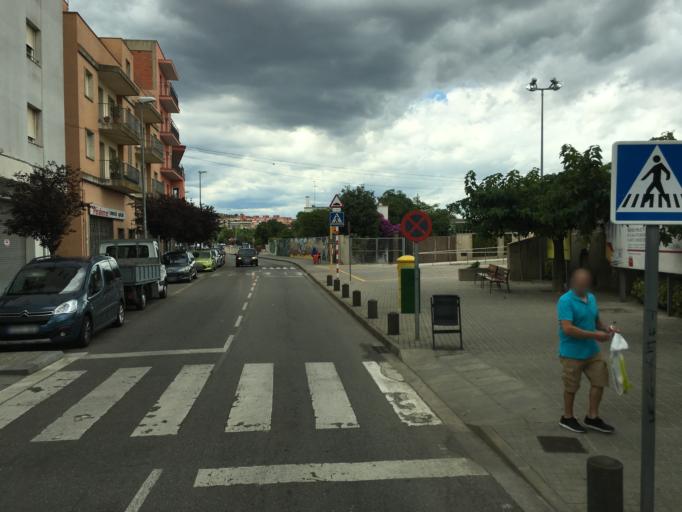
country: ES
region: Catalonia
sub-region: Provincia de Girona
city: Figueres
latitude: 42.2702
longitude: 2.9633
